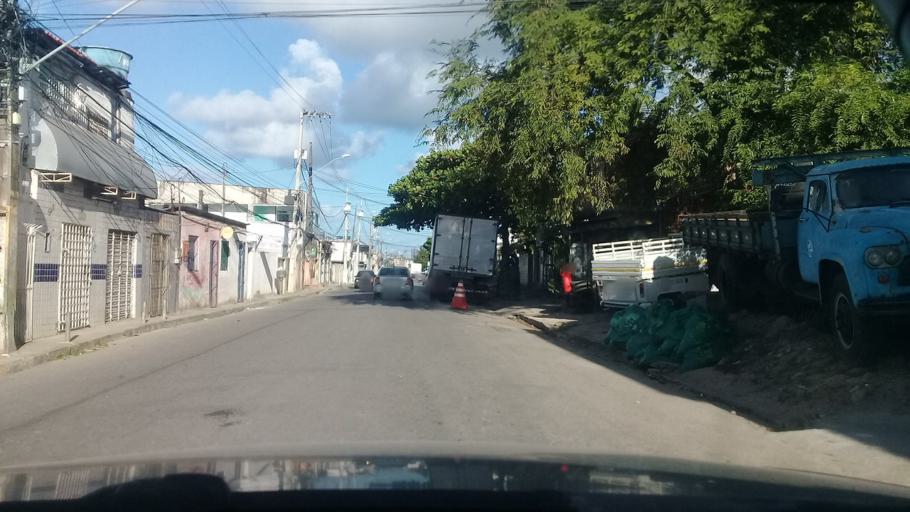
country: BR
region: Pernambuco
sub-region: Jaboatao Dos Guararapes
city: Jaboatao dos Guararapes
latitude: -8.1197
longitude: -34.9391
